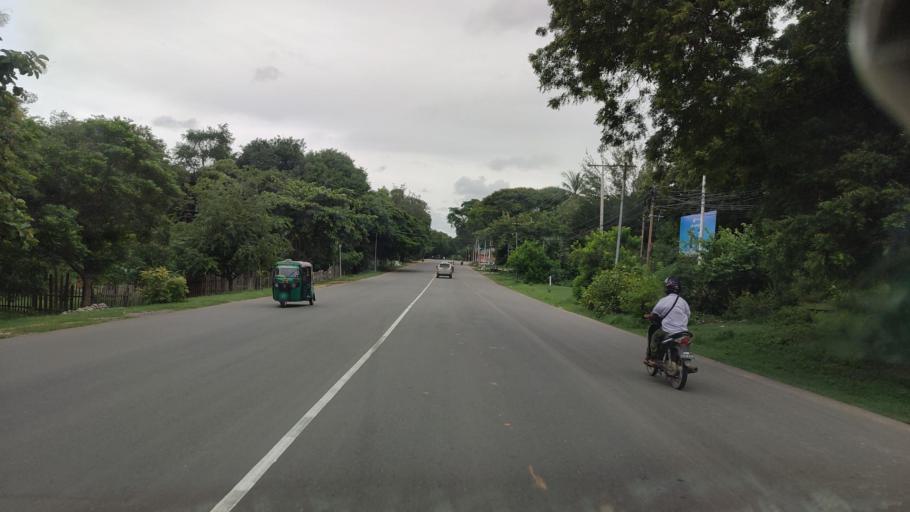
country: MM
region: Mandalay
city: Meiktila
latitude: 20.8700
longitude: 95.8681
